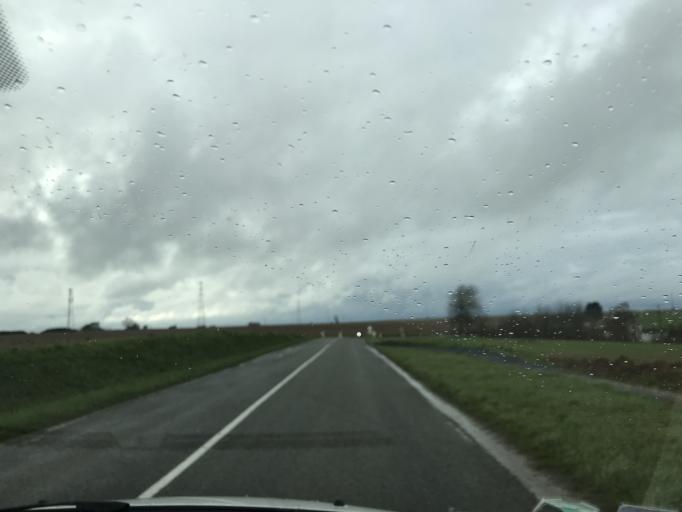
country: FR
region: Picardie
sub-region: Departement de l'Aisne
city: Billy-sur-Aisne
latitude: 49.3443
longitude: 3.3713
